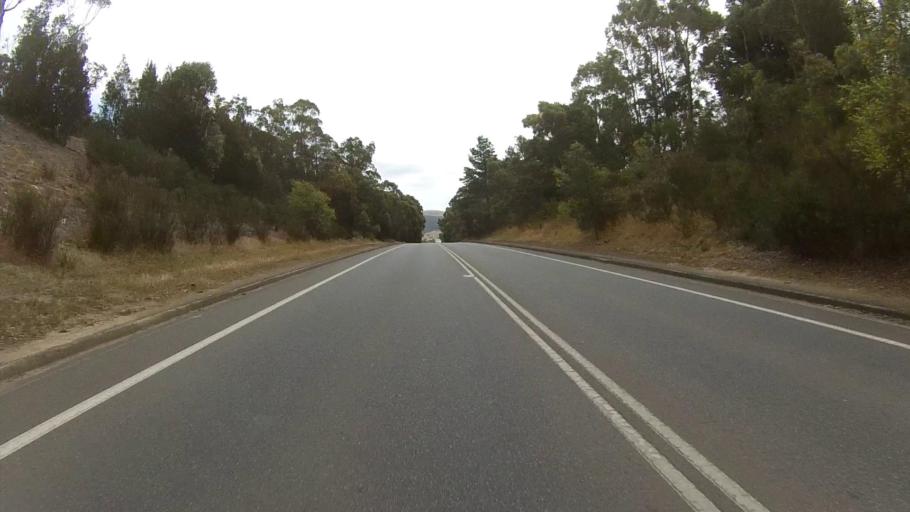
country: AU
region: Tasmania
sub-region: Kingborough
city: Blackmans Bay
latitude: -42.9977
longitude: 147.3098
